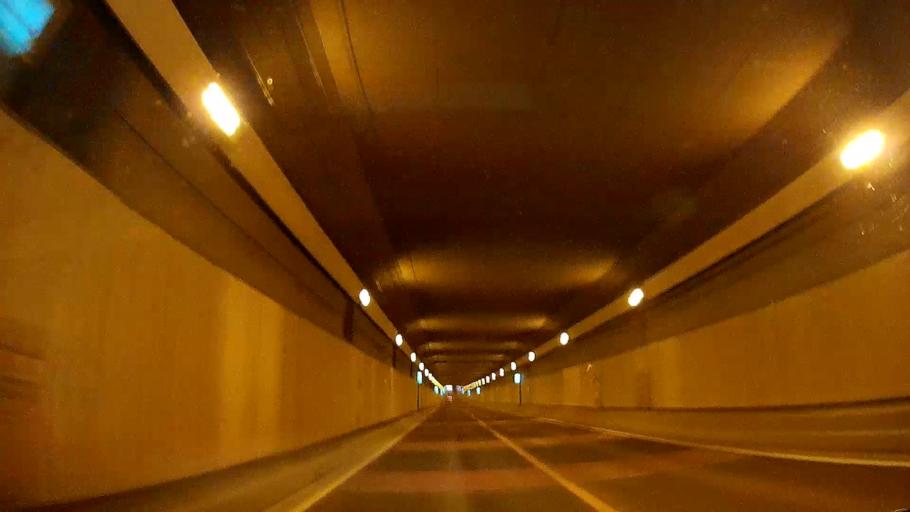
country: JP
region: Kanagawa
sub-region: Kawasaki-shi
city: Kawasaki
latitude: 35.6044
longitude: 139.7925
